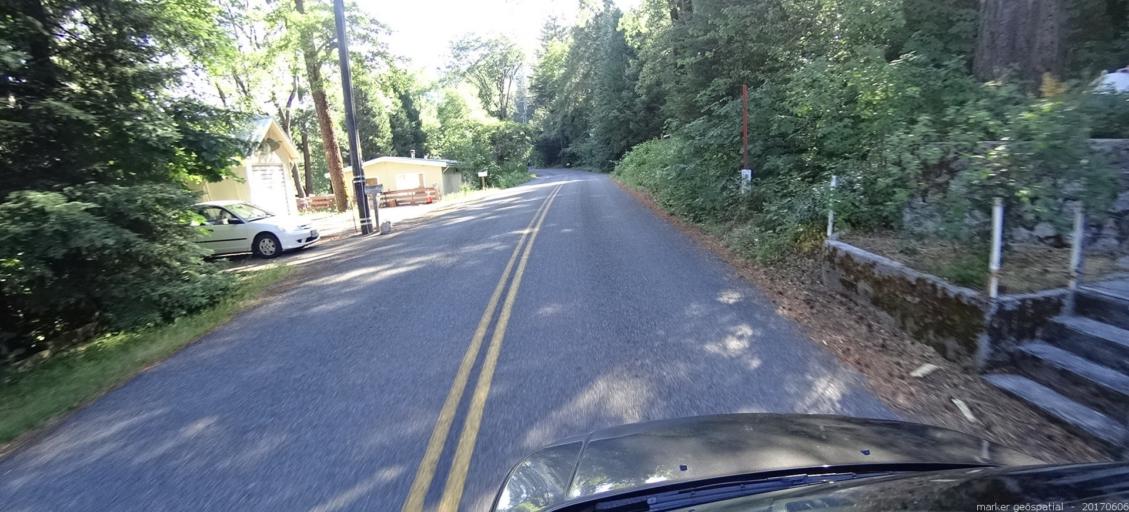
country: US
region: California
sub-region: Siskiyou County
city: Dunsmuir
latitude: 41.1951
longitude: -122.2770
